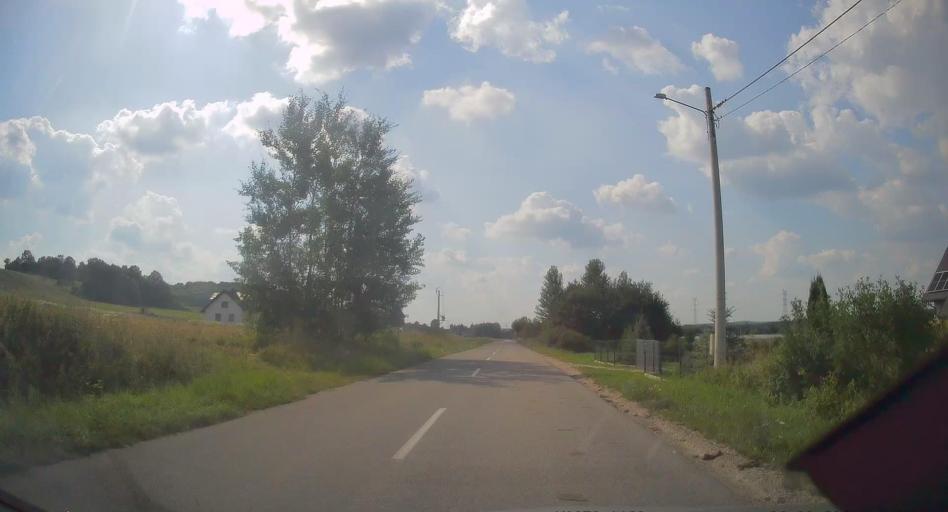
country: PL
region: Swietokrzyskie
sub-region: Powiat jedrzejowski
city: Malogoszcz
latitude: 50.8619
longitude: 20.3409
